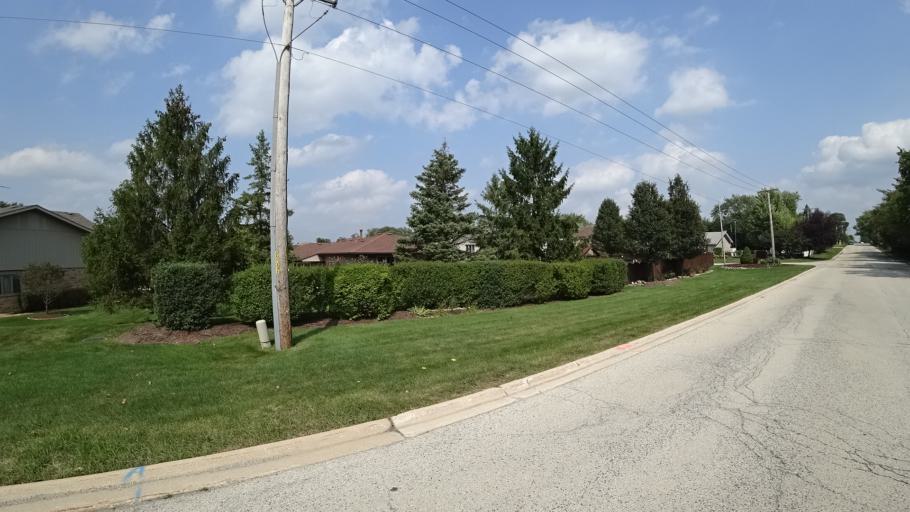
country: US
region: Illinois
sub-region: Will County
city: Goodings Grove
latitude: 41.6368
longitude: -87.9036
